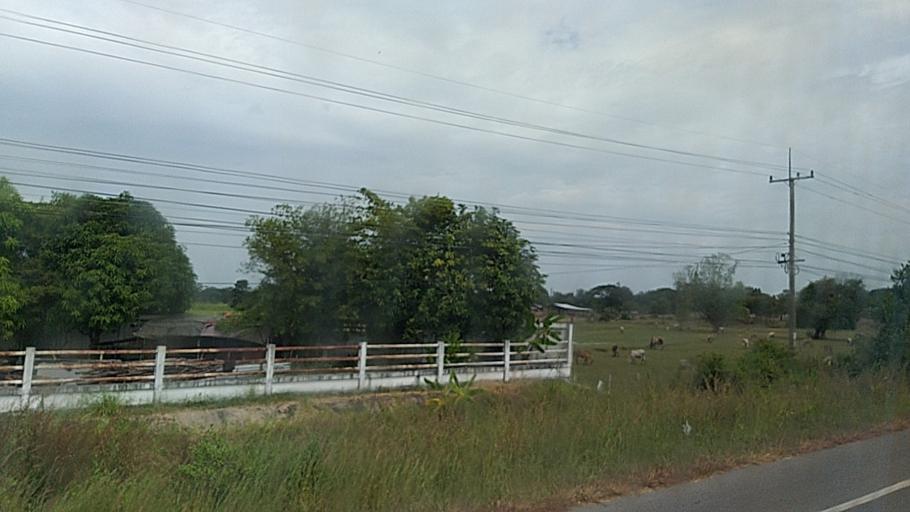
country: TH
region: Roi Et
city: Changhan
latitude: 16.0893
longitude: 103.5535
